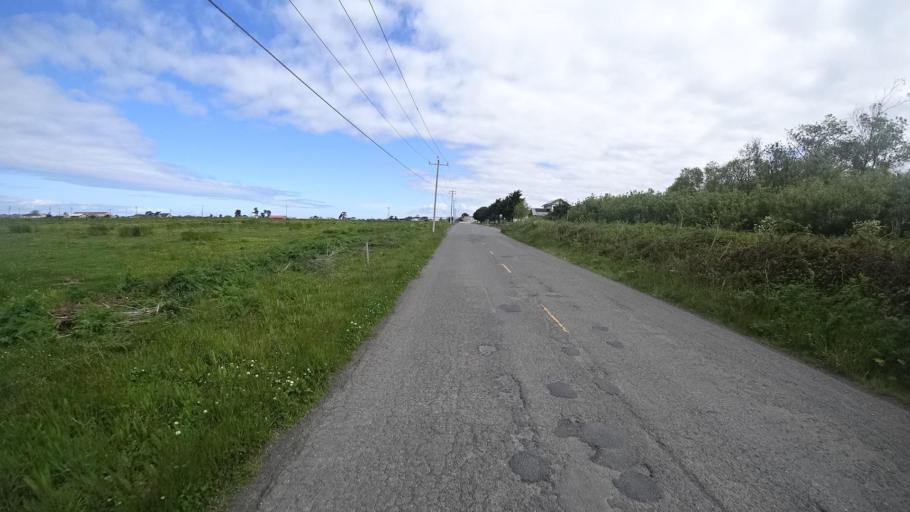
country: US
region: California
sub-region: Humboldt County
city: Arcata
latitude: 40.8696
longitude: -124.1060
